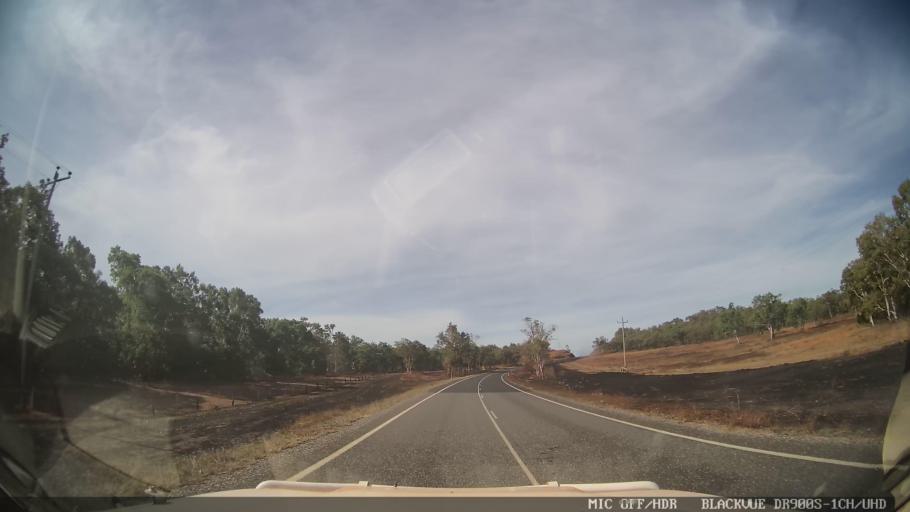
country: AU
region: Queensland
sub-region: Cook
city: Cooktown
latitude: -15.5995
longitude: 145.2258
